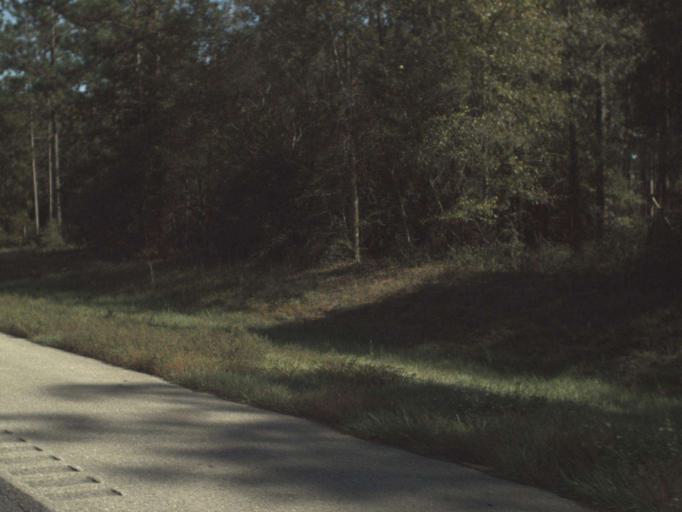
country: US
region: Florida
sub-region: Washington County
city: Chipley
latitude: 30.7460
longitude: -85.4989
